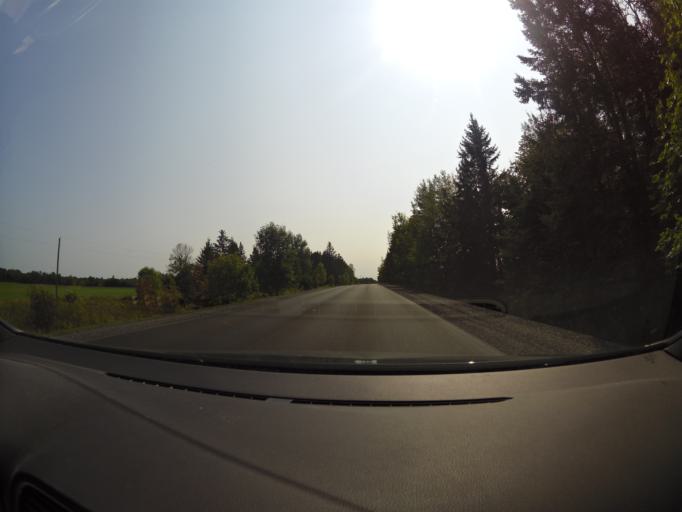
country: CA
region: Ontario
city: Arnprior
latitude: 45.4898
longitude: -76.1919
